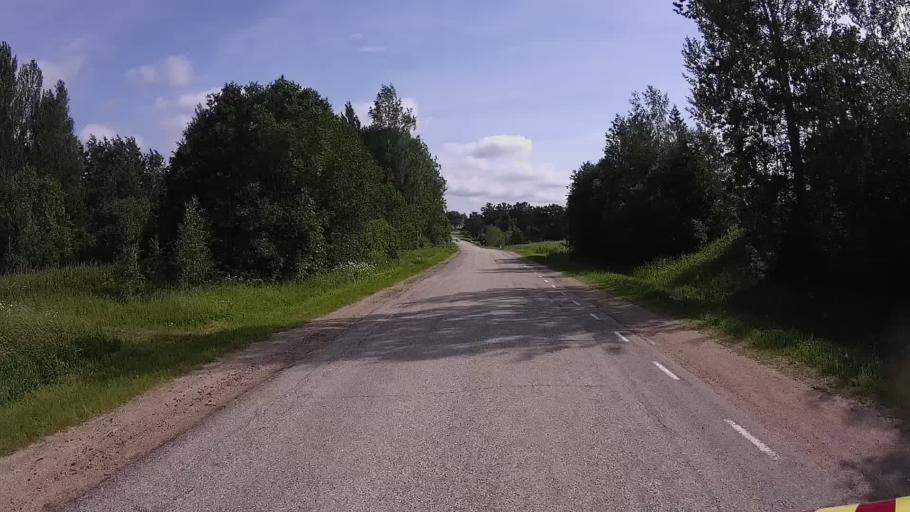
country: EE
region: Vorumaa
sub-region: Antsla vald
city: Vana-Antsla
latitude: 57.8585
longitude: 26.6025
